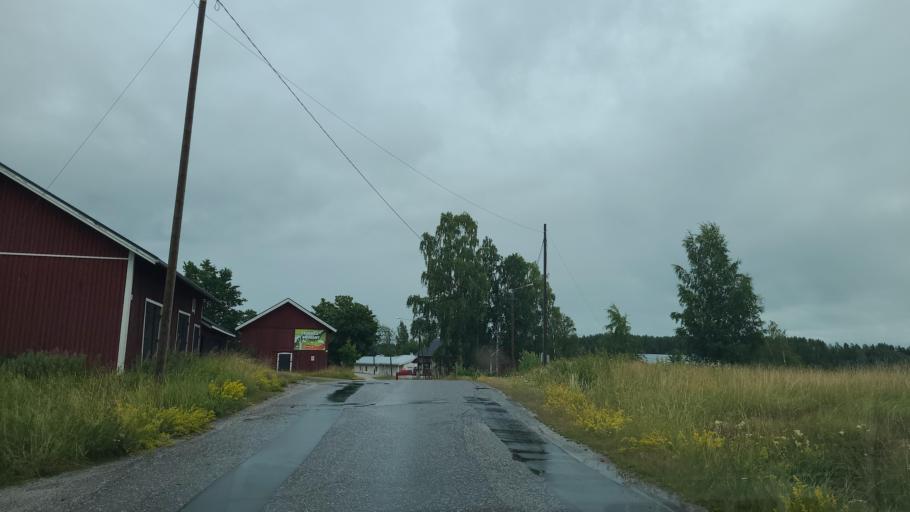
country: FI
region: Varsinais-Suomi
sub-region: Aboland-Turunmaa
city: Kimito
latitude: 60.1710
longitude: 22.7501
